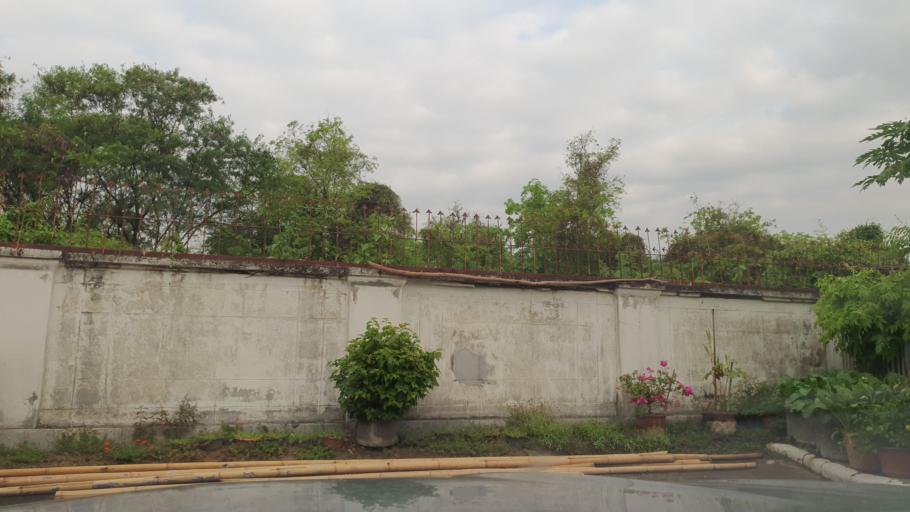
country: TH
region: Chiang Mai
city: Hang Dong
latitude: 18.6989
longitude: 98.9458
